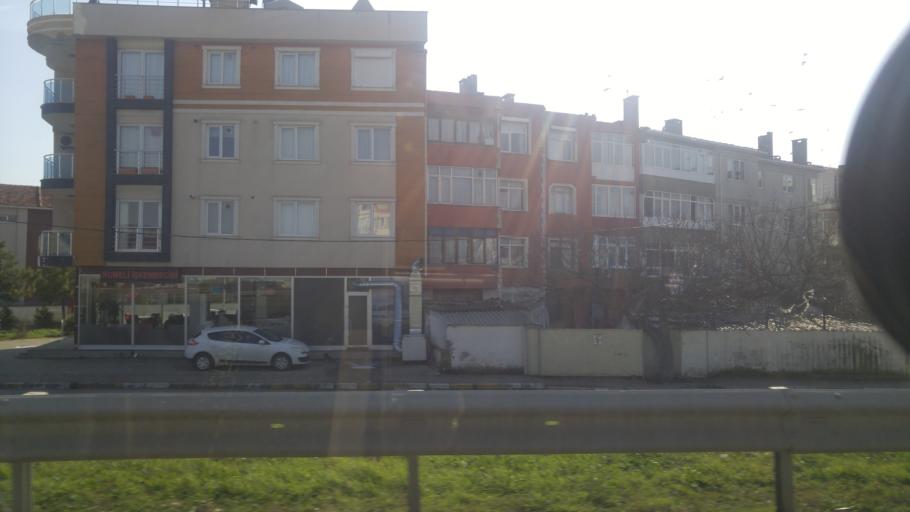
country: TR
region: Istanbul
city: Selimpasa
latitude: 41.0544
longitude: 28.3752
